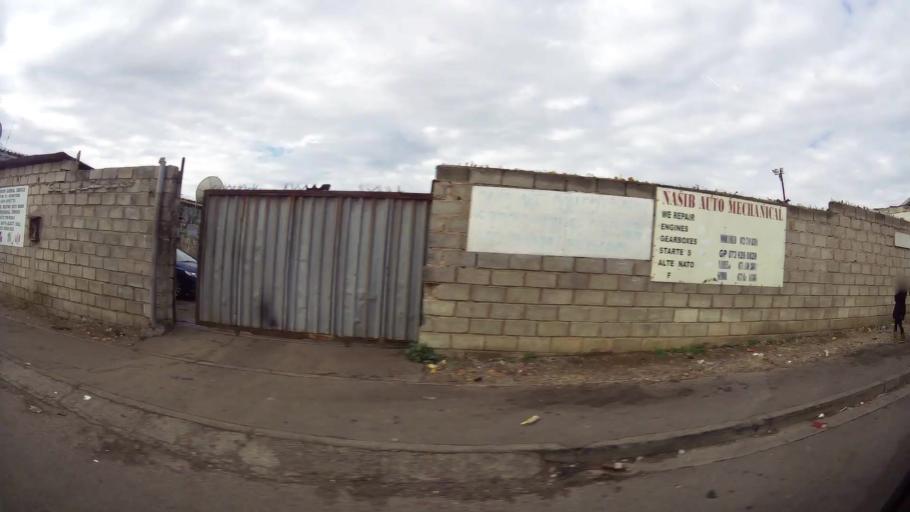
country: ZA
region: Eastern Cape
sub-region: Nelson Mandela Bay Metropolitan Municipality
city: Port Elizabeth
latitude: -33.9320
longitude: 25.5764
